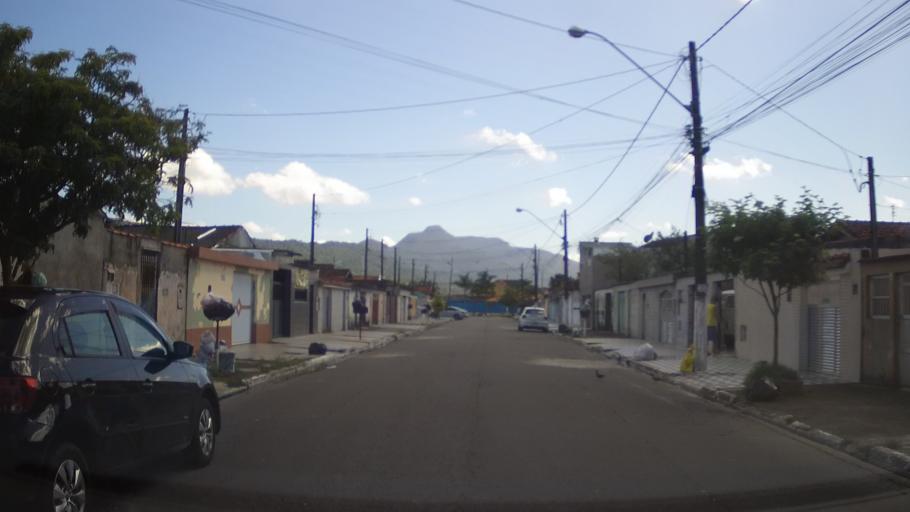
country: BR
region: Sao Paulo
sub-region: Mongagua
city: Mongagua
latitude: -24.0326
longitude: -46.5308
